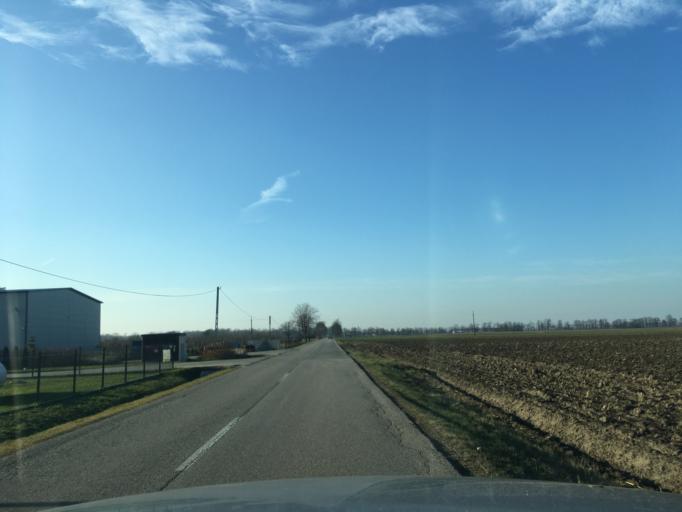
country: PL
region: Masovian Voivodeship
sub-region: Powiat pruszkowski
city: Nadarzyn
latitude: 52.0428
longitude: 20.8064
